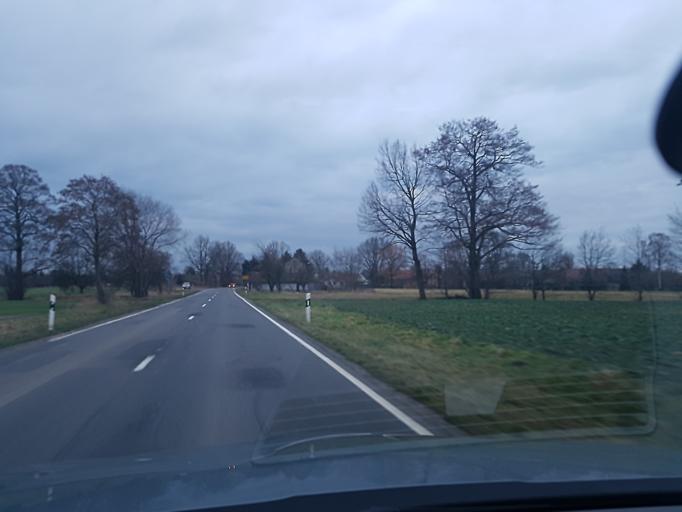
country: DE
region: Brandenburg
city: Schonewalde
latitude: 51.6626
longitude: 13.5900
